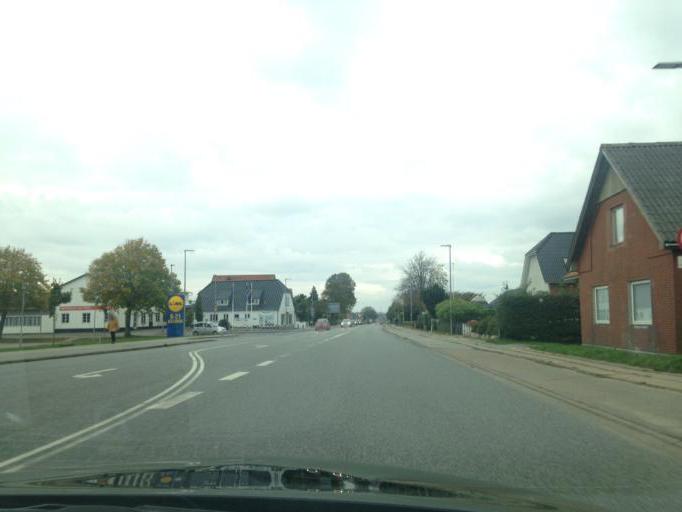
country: DK
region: South Denmark
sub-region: Kolding Kommune
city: Kolding
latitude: 55.4711
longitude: 9.4707
